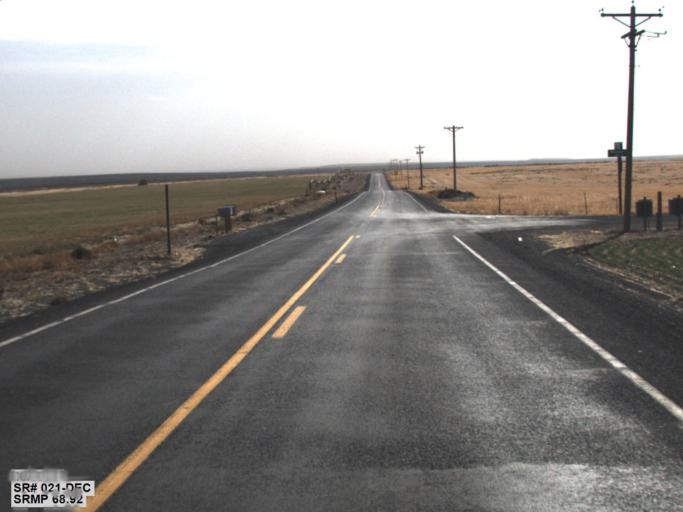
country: US
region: Washington
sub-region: Okanogan County
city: Coulee Dam
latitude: 47.4801
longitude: -118.7849
